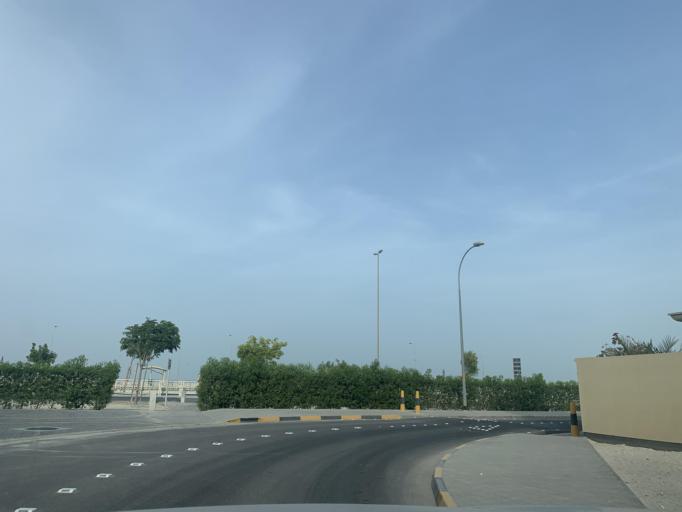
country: BH
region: Muharraq
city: Al Muharraq
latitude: 26.3169
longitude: 50.6309
